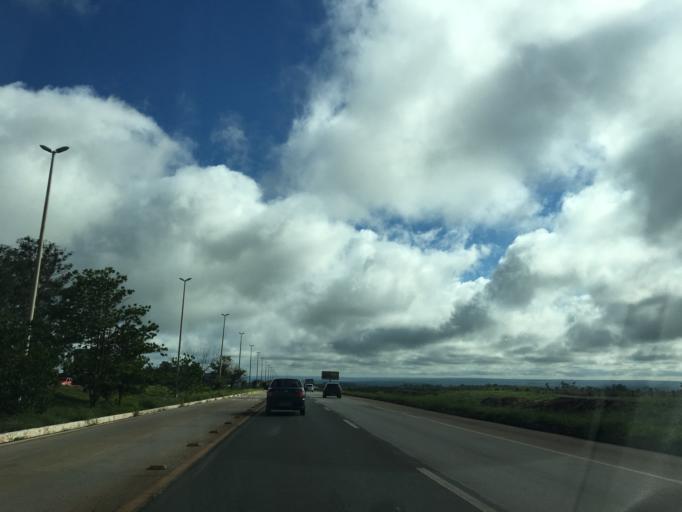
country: BR
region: Federal District
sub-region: Brasilia
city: Brasilia
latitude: -15.9597
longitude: -48.0134
